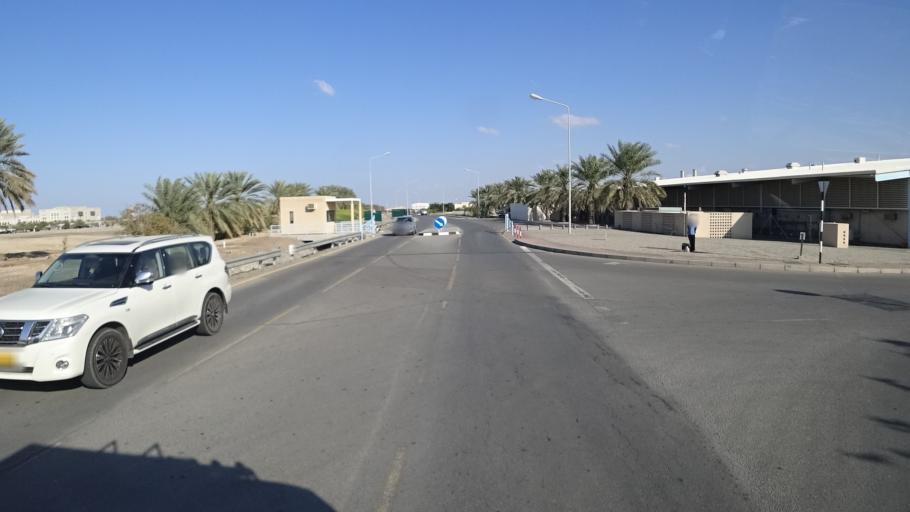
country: OM
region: Muhafazat Masqat
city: As Sib al Jadidah
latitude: 23.5870
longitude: 58.1735
